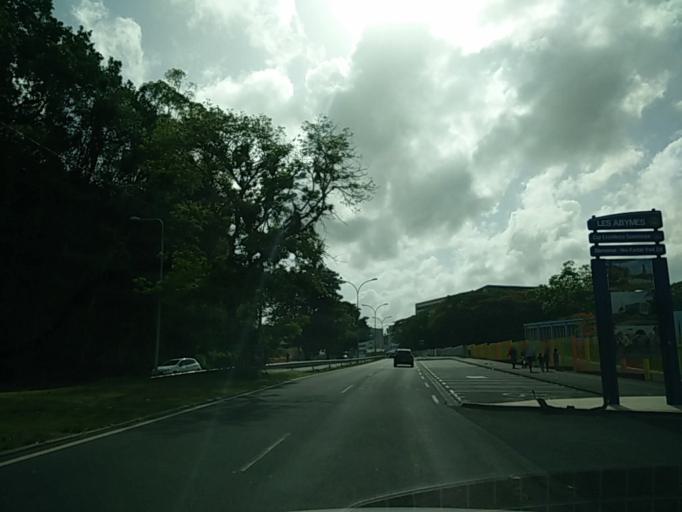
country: GP
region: Guadeloupe
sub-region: Guadeloupe
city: Pointe-a-Pitre
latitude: 16.2482
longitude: -61.5267
